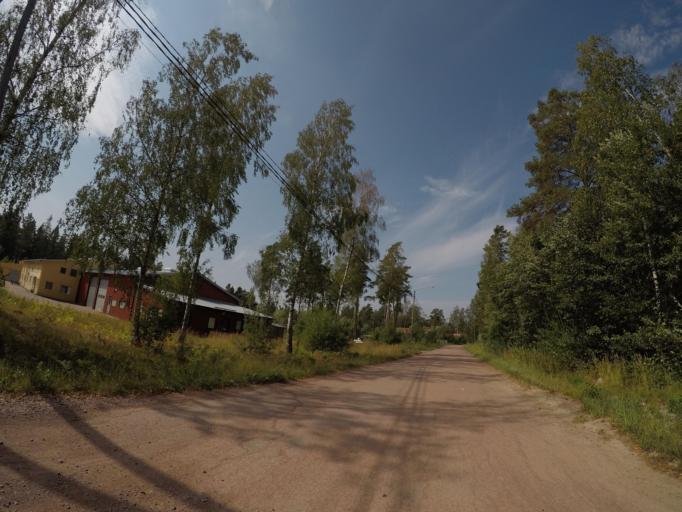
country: AX
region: Alands landsbygd
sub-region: Finstroem
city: Finstroem
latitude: 60.2334
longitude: 19.9765
